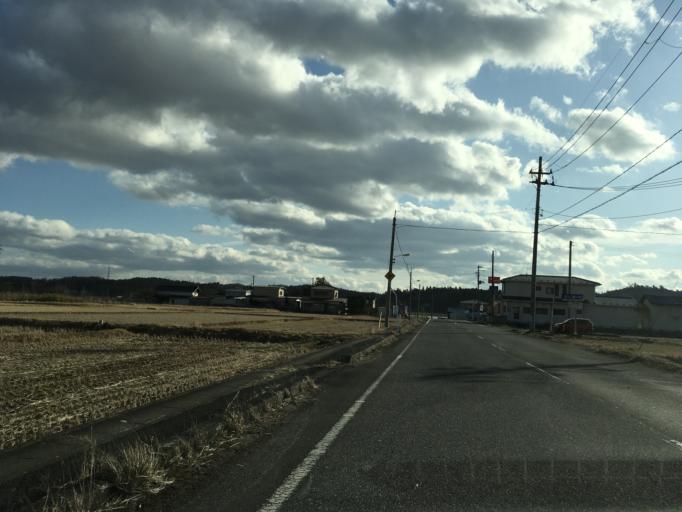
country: JP
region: Iwate
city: Ichinoseki
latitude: 38.8284
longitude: 140.9990
